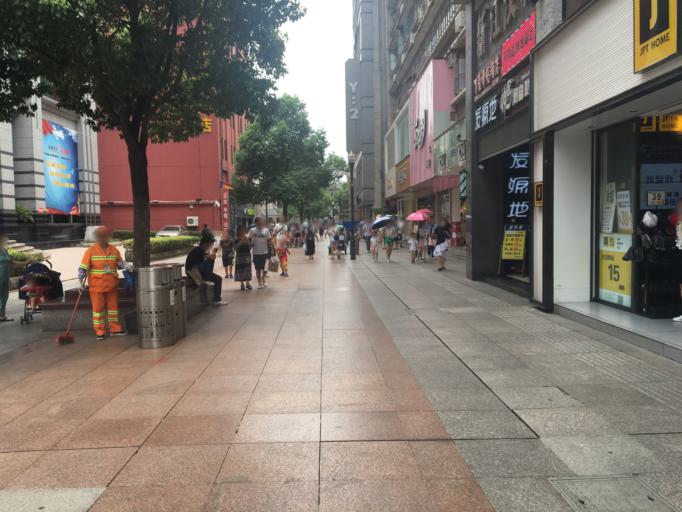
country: CN
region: Hubei
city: Wuhan
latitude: 30.5802
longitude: 114.2899
